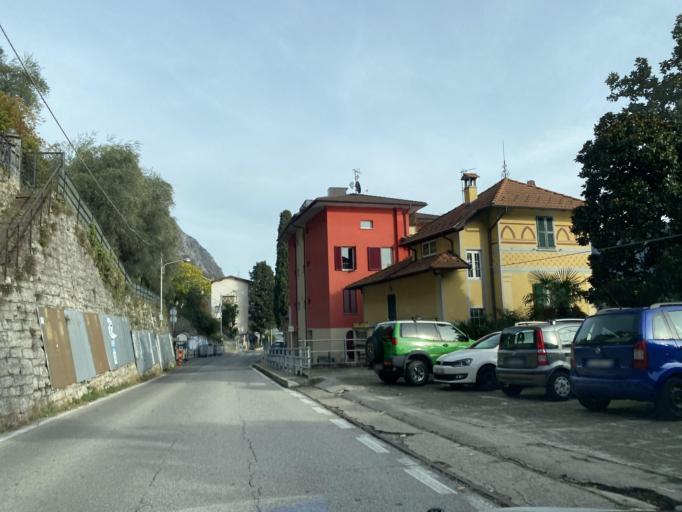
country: IT
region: Lombardy
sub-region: Provincia di Como
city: San Mamete
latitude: 46.0227
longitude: 9.0379
